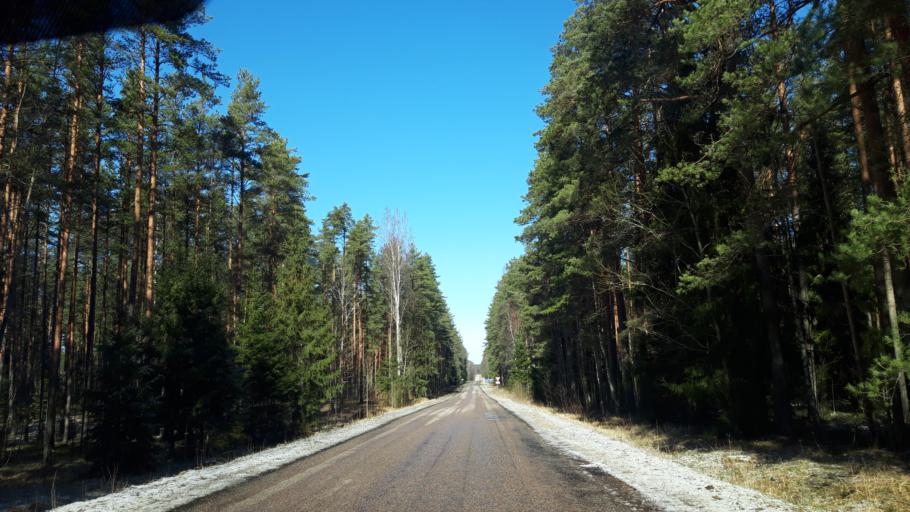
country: LV
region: Strenci
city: Strenci
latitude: 57.5972
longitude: 25.7182
